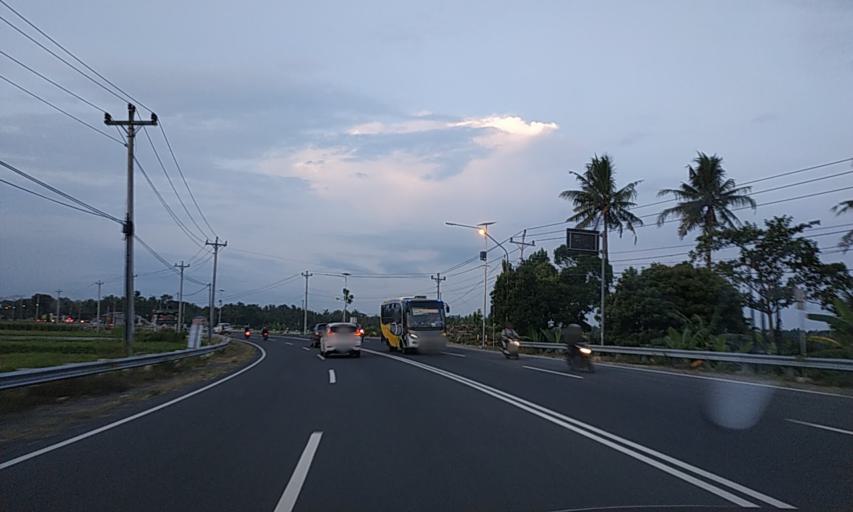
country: ID
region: Daerah Istimewa Yogyakarta
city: Srandakan
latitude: -7.8752
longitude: 110.2073
